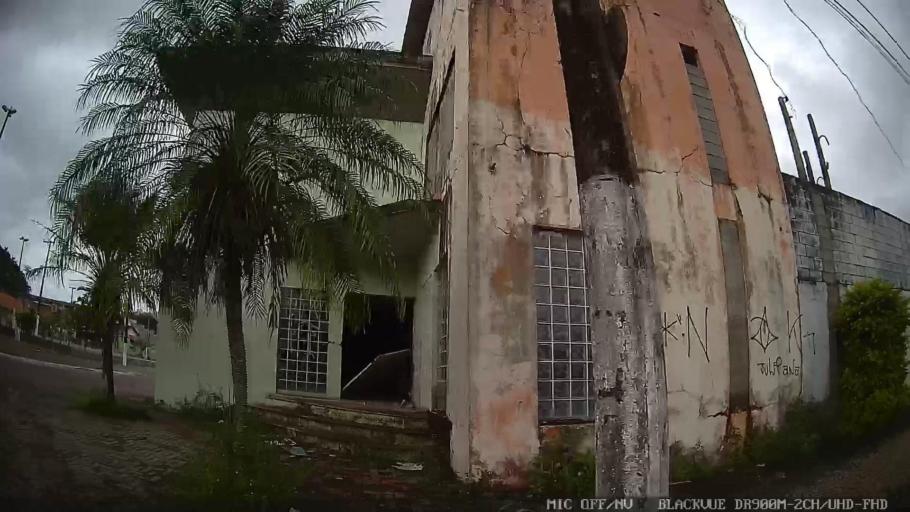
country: BR
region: Sao Paulo
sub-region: Itanhaem
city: Itanhaem
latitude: -24.1919
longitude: -46.8070
